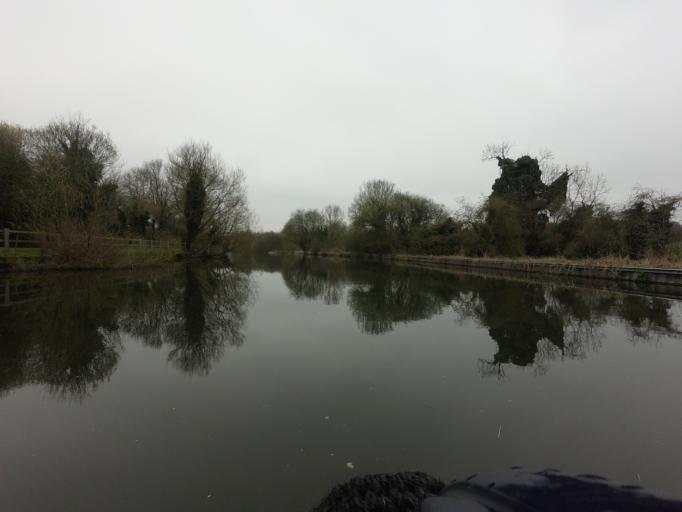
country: GB
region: England
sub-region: Hertfordshire
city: Abbots Langley
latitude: 51.6851
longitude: -0.4337
